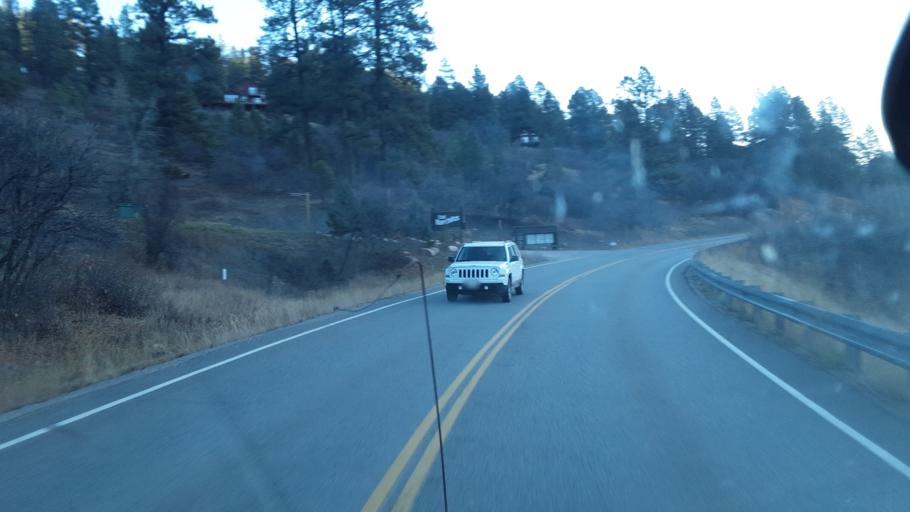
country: US
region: Colorado
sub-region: La Plata County
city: Bayfield
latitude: 37.3536
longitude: -107.6888
